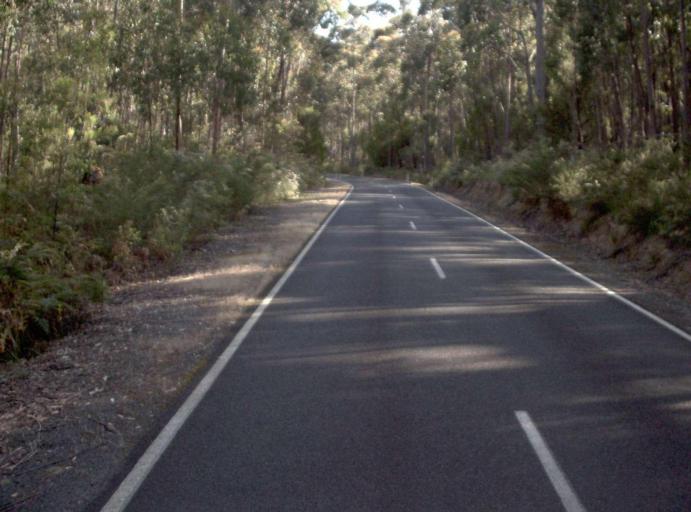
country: AU
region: Victoria
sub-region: East Gippsland
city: Lakes Entrance
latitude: -37.5953
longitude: 148.5287
